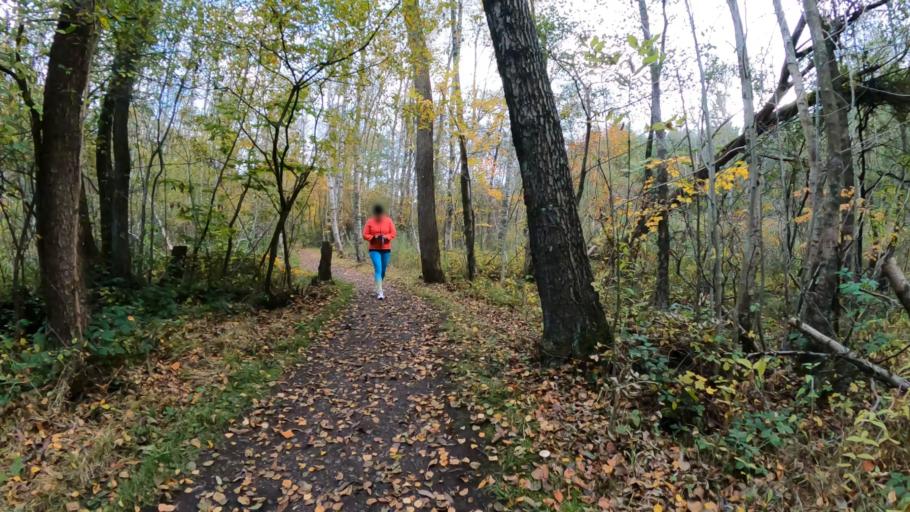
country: DE
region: Schleswig-Holstein
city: Ahrensburg
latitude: 53.6651
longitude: 10.2122
